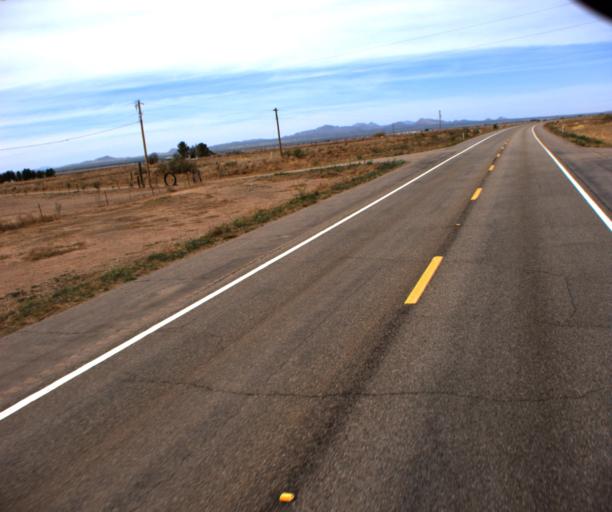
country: US
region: Arizona
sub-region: Cochise County
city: Pirtleville
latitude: 31.5542
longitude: -109.6641
